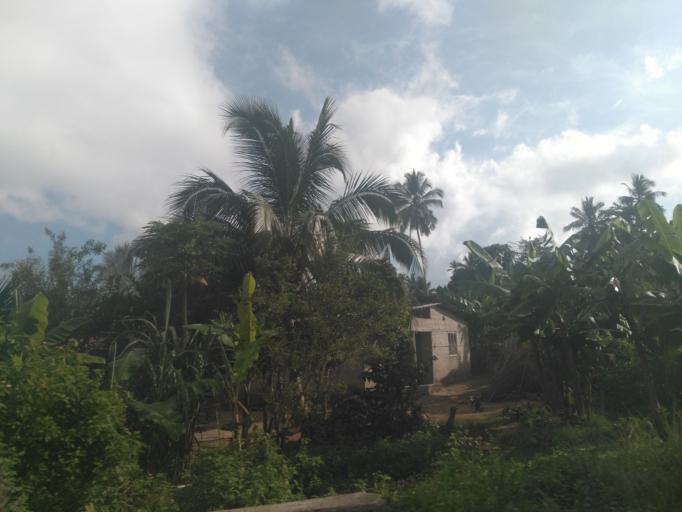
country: TZ
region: Zanzibar Central/South
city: Koani
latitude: -6.1089
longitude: 39.2982
